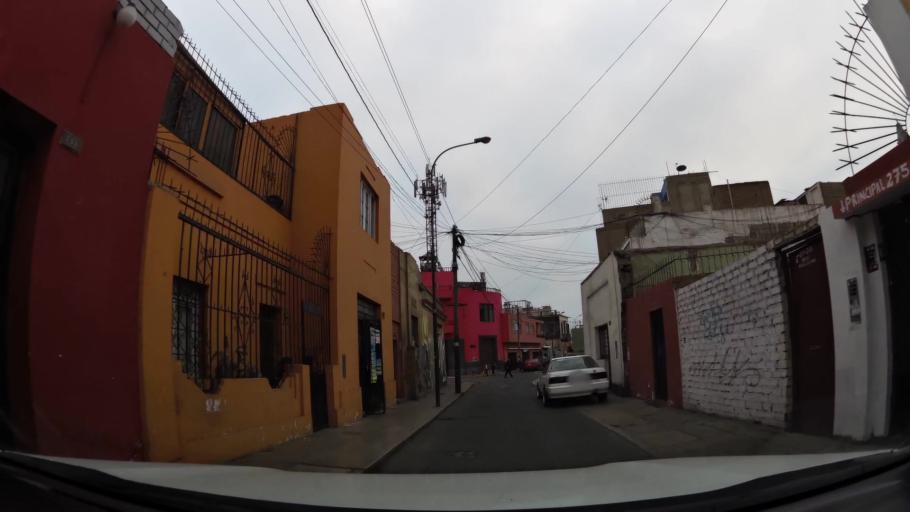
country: PE
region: Lima
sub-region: Lima
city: Surco
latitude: -12.1463
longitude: -77.0198
